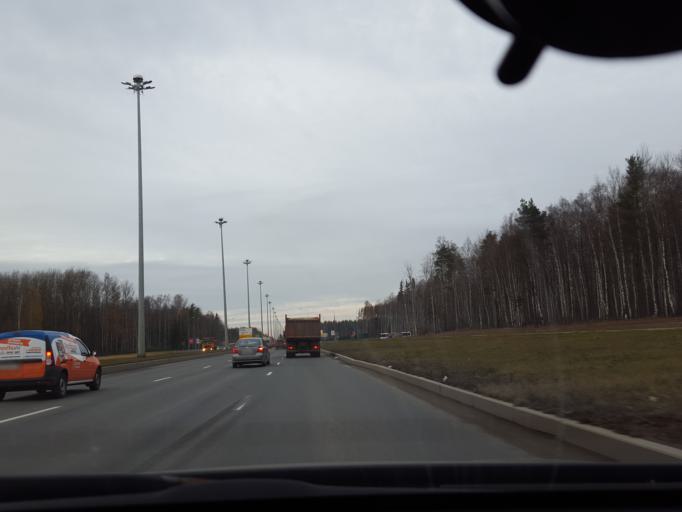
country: RU
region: Leningrad
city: Untolovo
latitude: 60.0462
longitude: 30.2350
